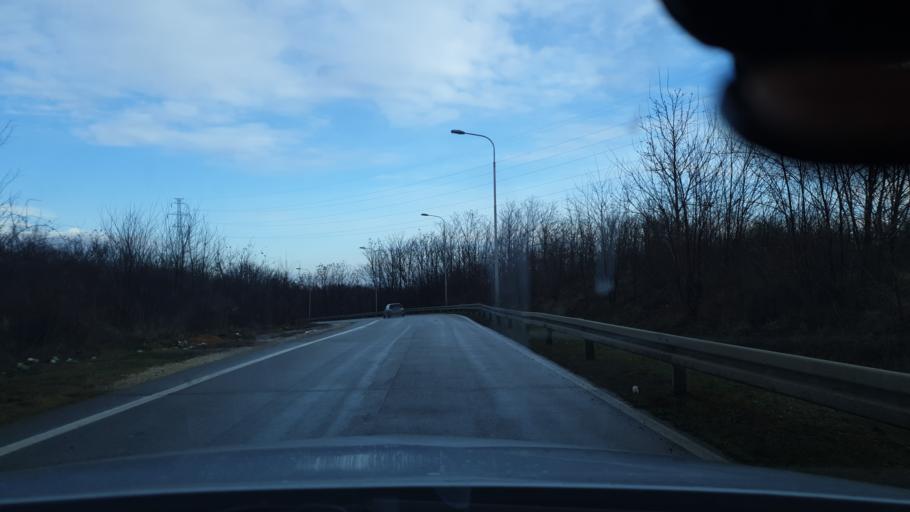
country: RS
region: Central Serbia
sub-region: Podunavski Okrug
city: Smederevo
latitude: 44.6076
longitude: 20.9553
